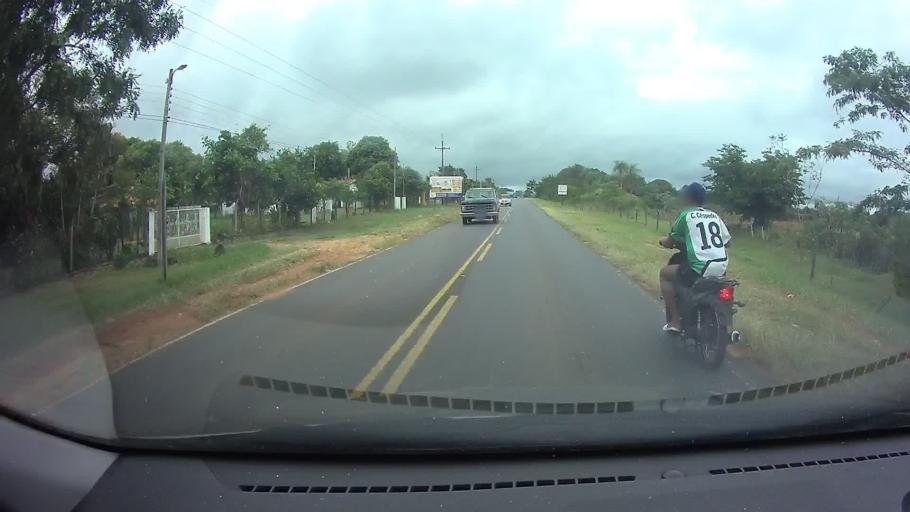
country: PY
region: Central
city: Guarambare
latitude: -25.5135
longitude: -57.4894
